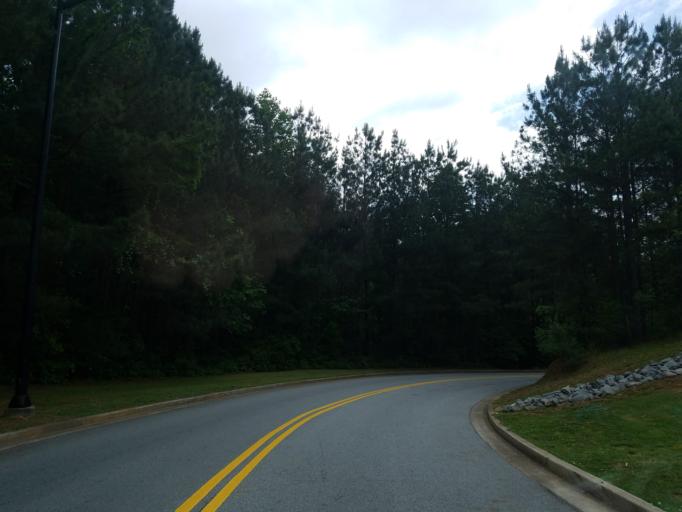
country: US
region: Georgia
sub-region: Cobb County
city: Fair Oaks
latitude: 33.9364
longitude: -84.5236
